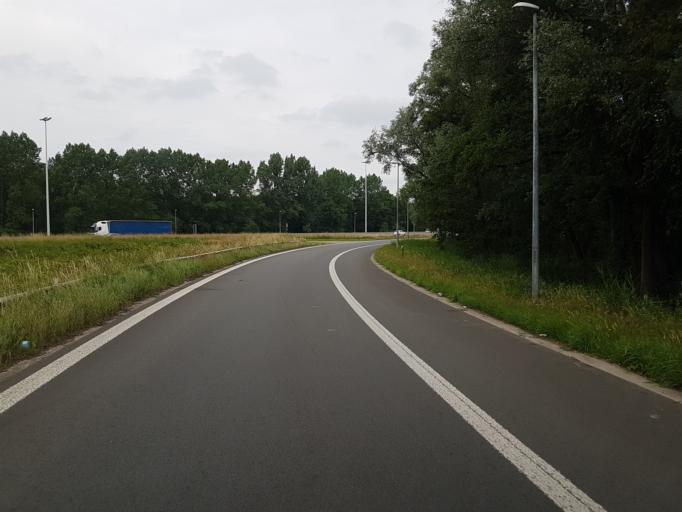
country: BE
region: Flanders
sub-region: Provincie Antwerpen
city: Lille
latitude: 51.2573
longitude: 4.8085
